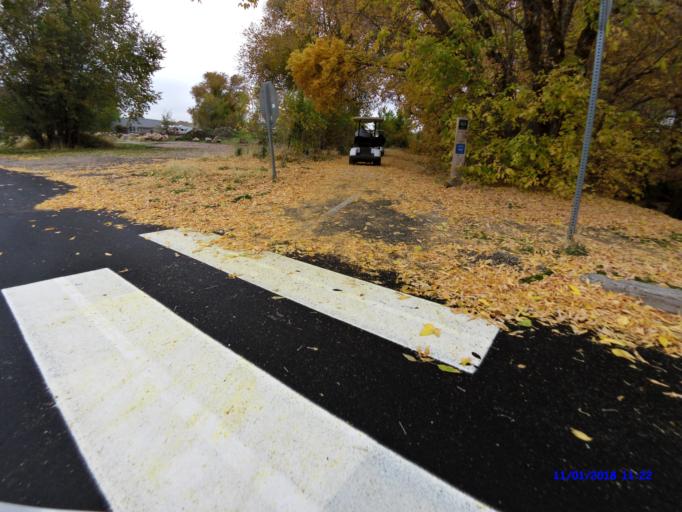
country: US
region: Utah
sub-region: Weber County
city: Ogden
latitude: 41.2343
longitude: -111.9758
